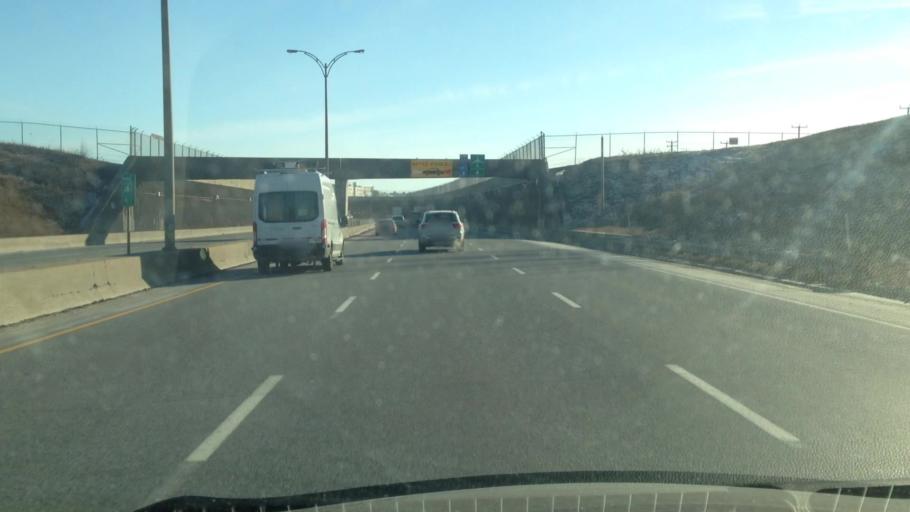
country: CA
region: Quebec
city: Dorval
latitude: 45.4811
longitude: -73.7216
